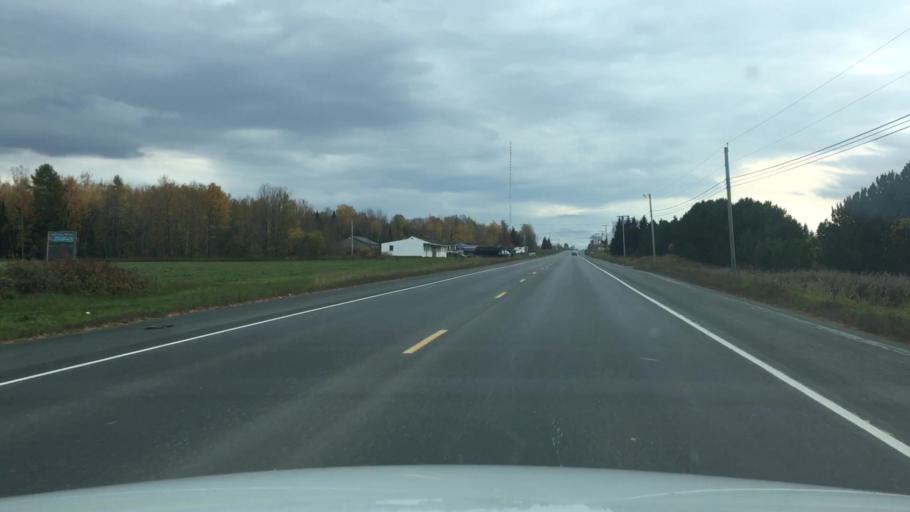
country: US
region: Maine
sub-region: Aroostook County
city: Caribou
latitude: 46.7733
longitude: -67.9895
